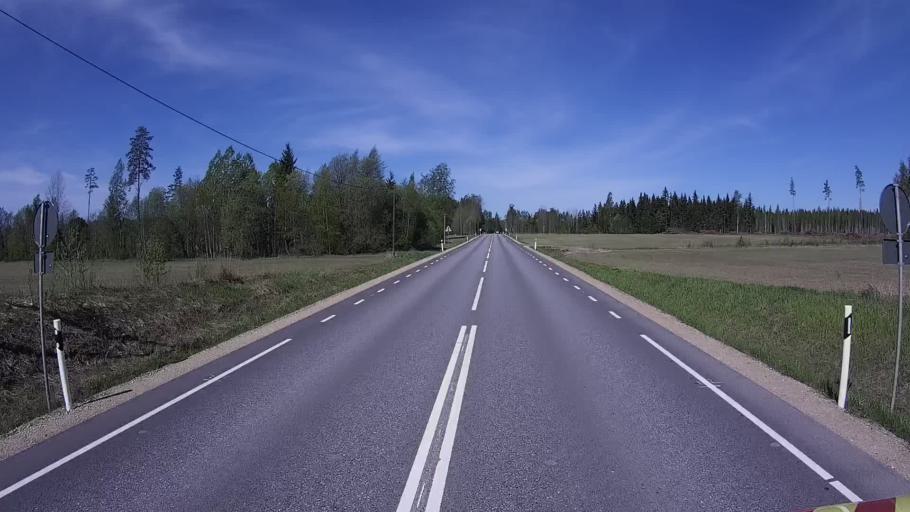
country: EE
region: Polvamaa
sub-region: Raepina vald
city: Rapina
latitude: 57.9787
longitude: 27.2857
